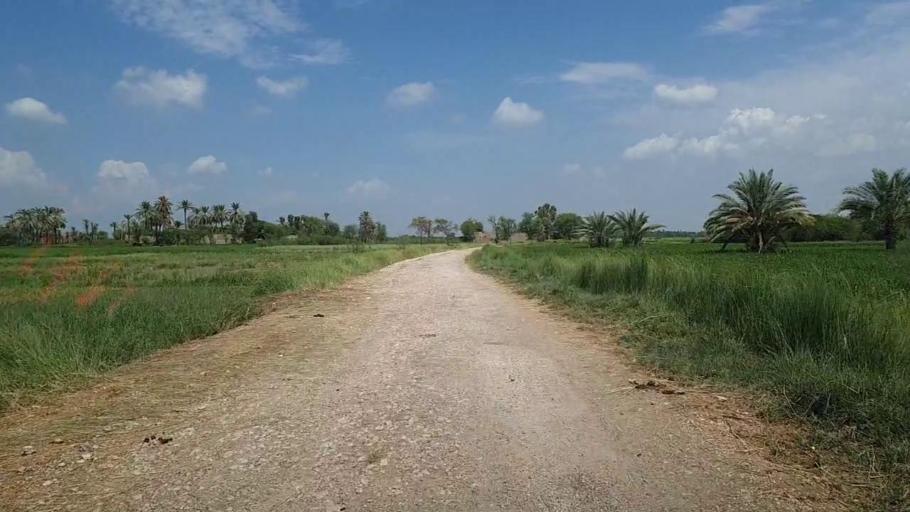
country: PK
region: Sindh
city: Bhiria
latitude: 26.9518
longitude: 68.2374
